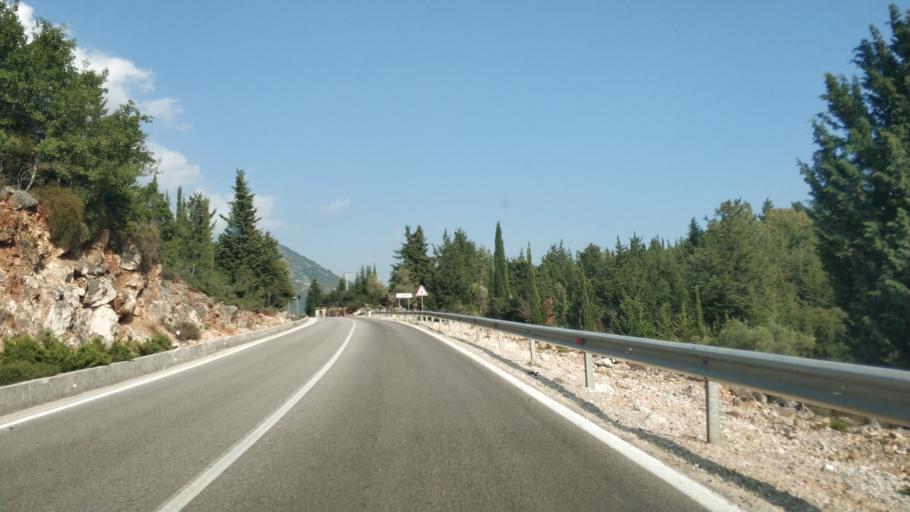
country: AL
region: Vlore
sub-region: Rrethi i Vlores
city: Vranisht
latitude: 40.1418
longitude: 19.6689
